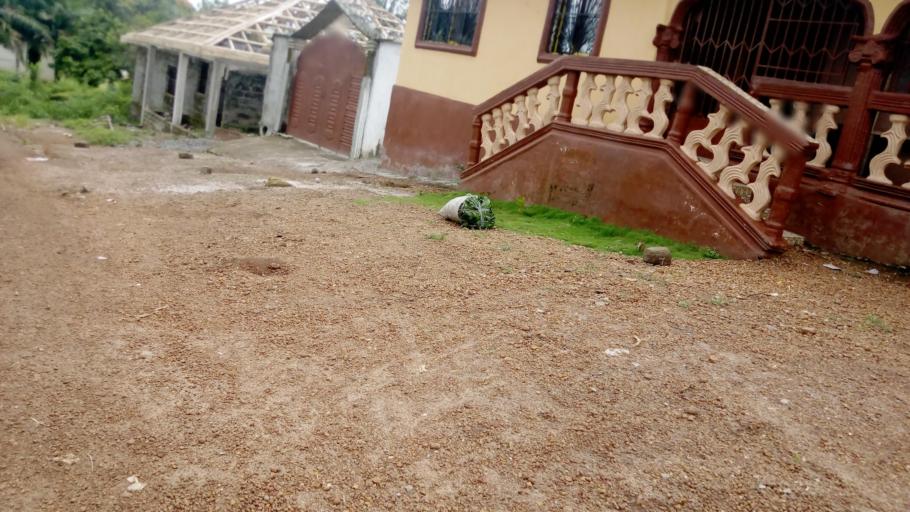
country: SL
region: Northern Province
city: Makeni
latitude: 8.8878
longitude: -12.0269
